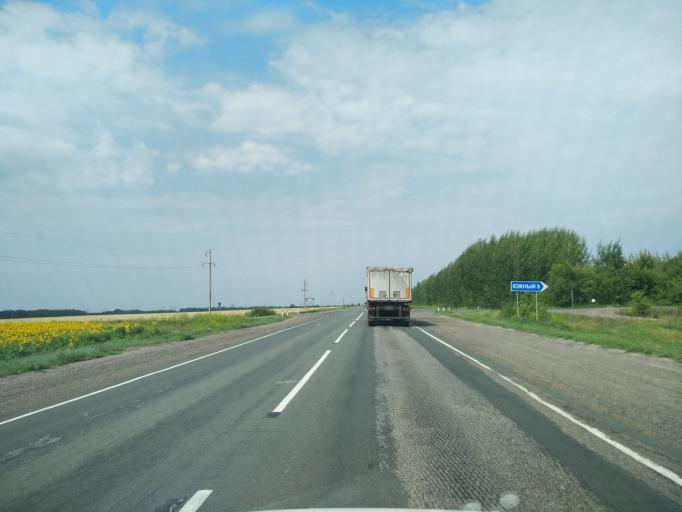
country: RU
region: Voronezj
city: Orlovo
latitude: 51.6769
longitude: 39.6945
